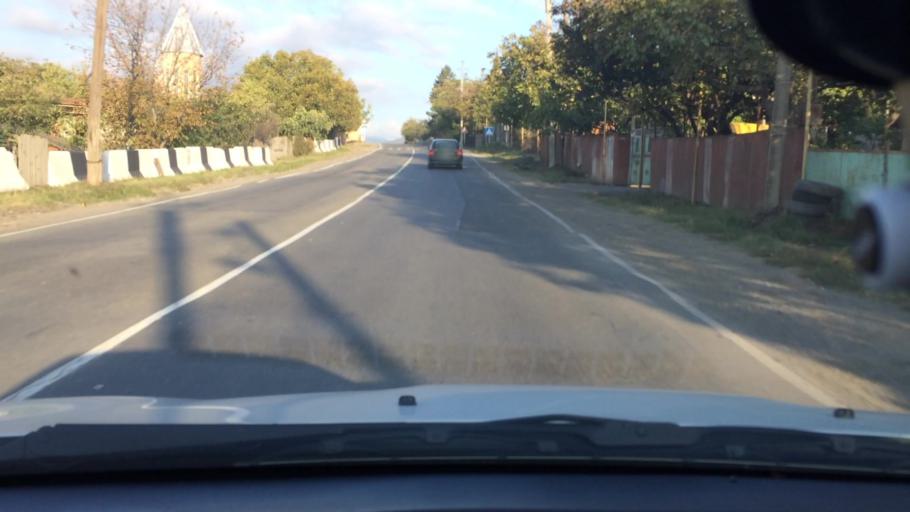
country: GE
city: Surami
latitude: 42.0166
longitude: 43.5701
